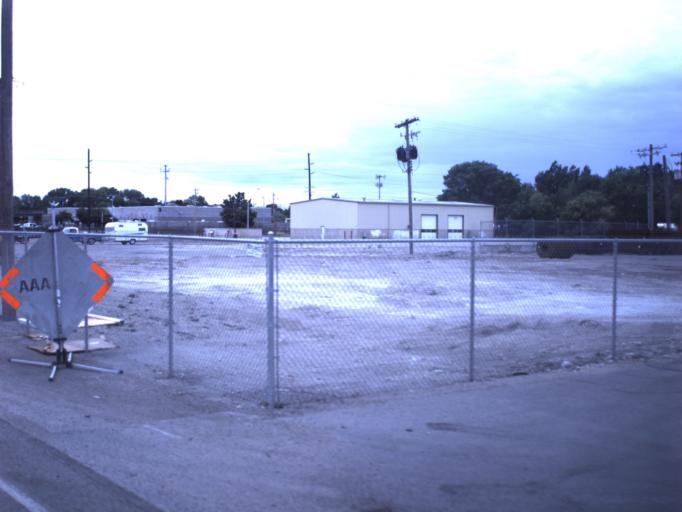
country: US
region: Utah
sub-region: Weber County
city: Ogden
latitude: 41.2386
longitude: -111.9786
